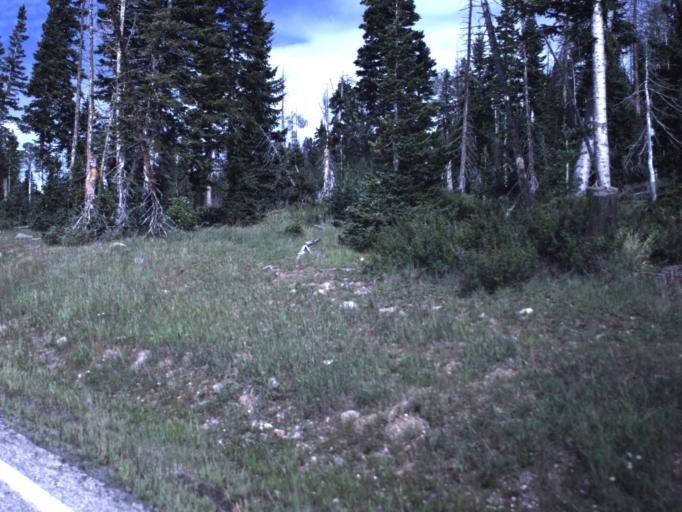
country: US
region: Utah
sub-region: Iron County
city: Cedar City
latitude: 37.5723
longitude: -112.8269
